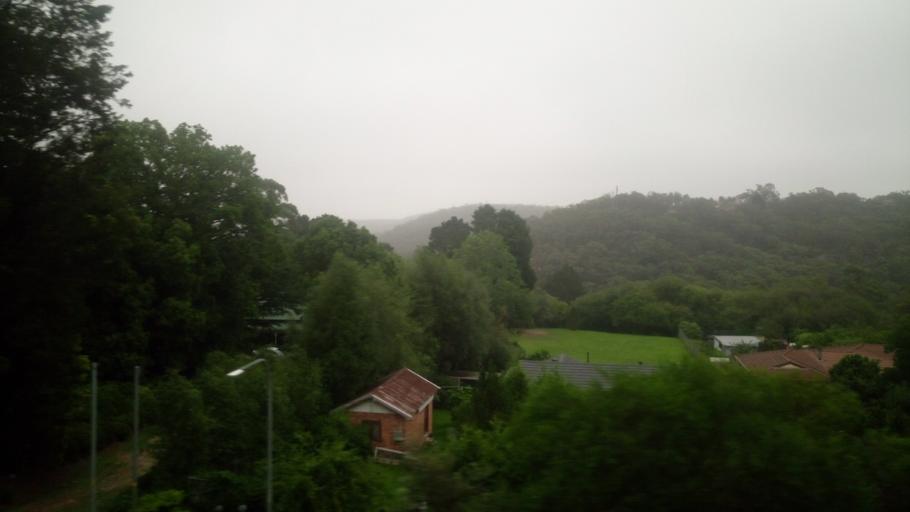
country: AU
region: New South Wales
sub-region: Blue Mountains Municipality
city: Lawson
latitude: -33.7193
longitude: 150.4392
